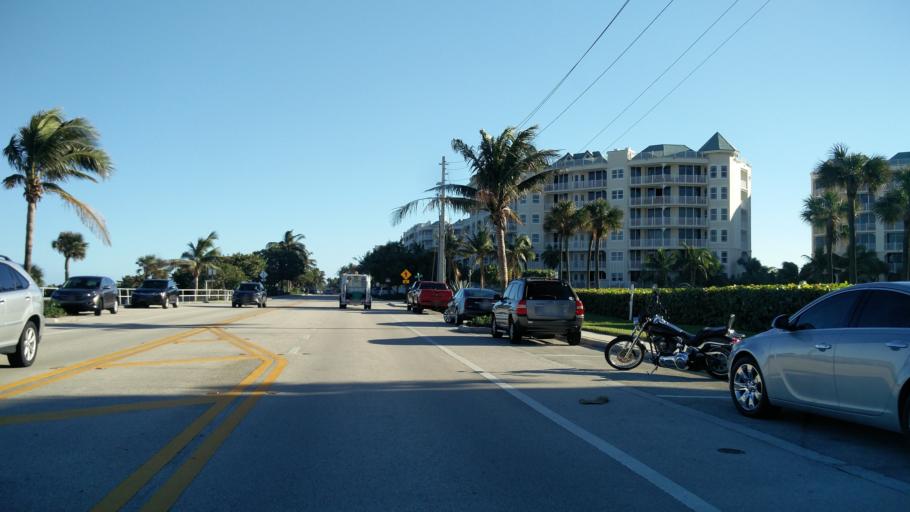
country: US
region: Florida
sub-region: Palm Beach County
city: Jupiter
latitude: 26.9211
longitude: -80.0664
